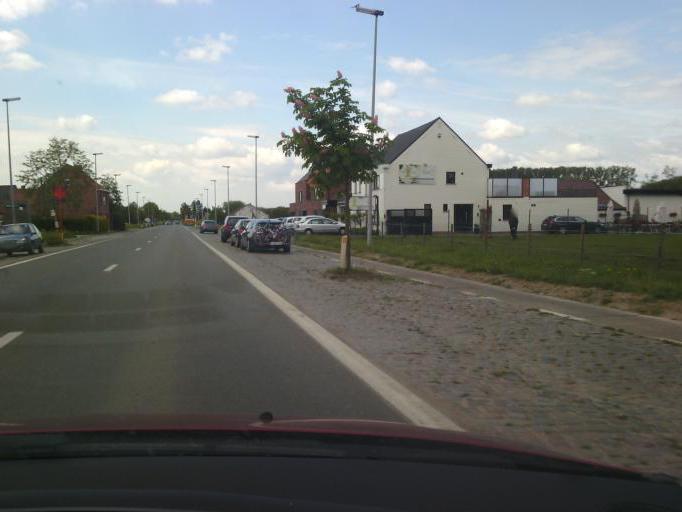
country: BE
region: Flanders
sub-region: Provincie Oost-Vlaanderen
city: Berlare
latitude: 51.0200
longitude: 4.0436
